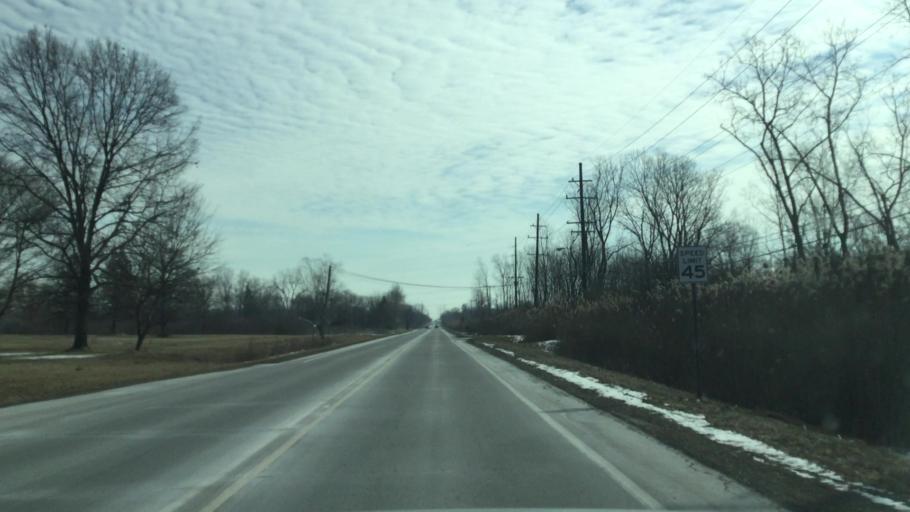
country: US
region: Michigan
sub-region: Wayne County
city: Flat Rock
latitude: 42.1381
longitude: -83.2891
